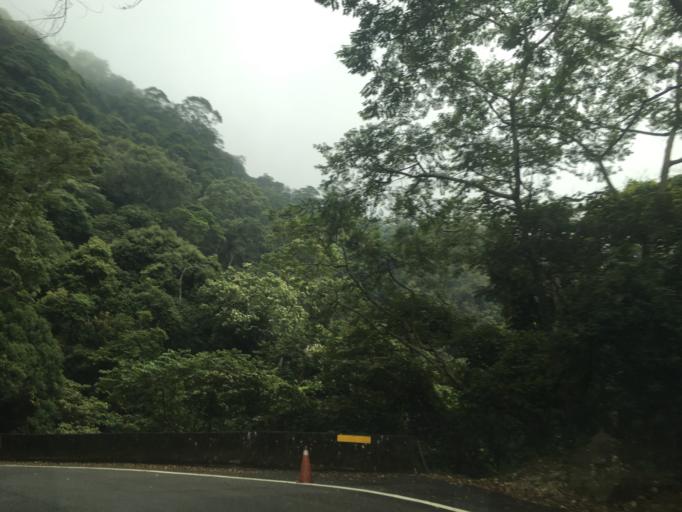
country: TW
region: Taiwan
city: Fengyuan
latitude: 24.2485
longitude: 120.9180
